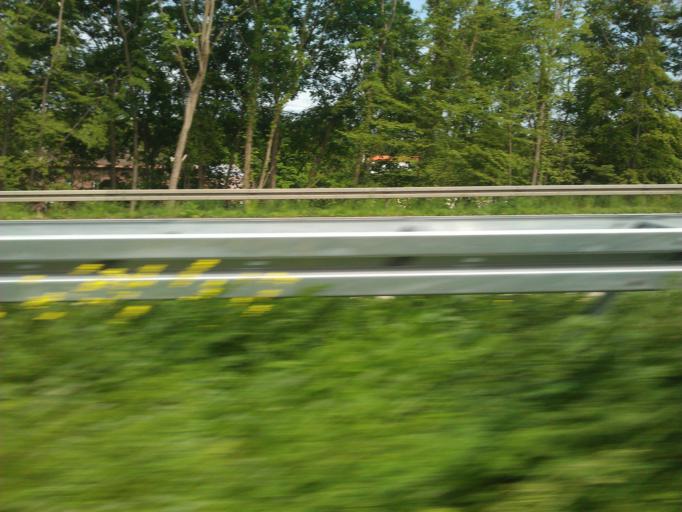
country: DE
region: North Rhine-Westphalia
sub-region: Regierungsbezirk Koln
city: Wurselen
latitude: 50.8043
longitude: 6.1117
